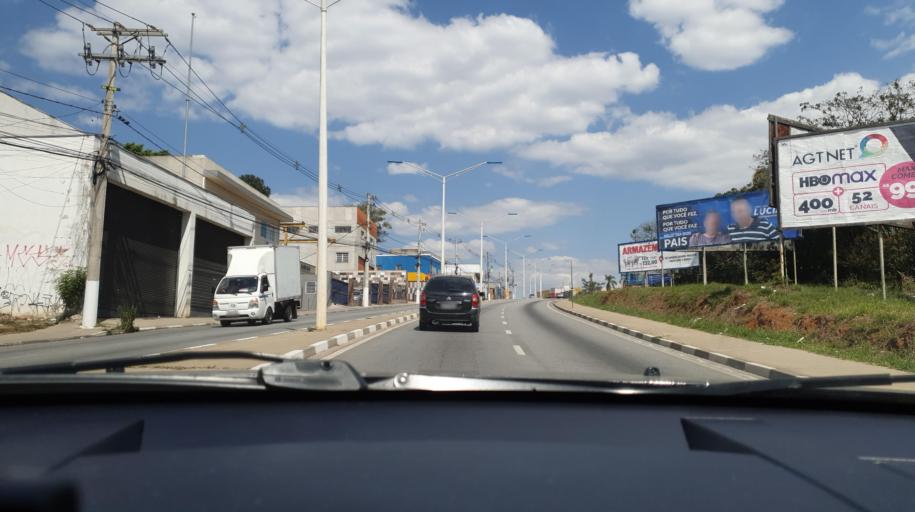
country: BR
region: Sao Paulo
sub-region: Vargem Grande Paulista
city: Vargem Grande Paulista
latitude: -23.6448
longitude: -46.9921
